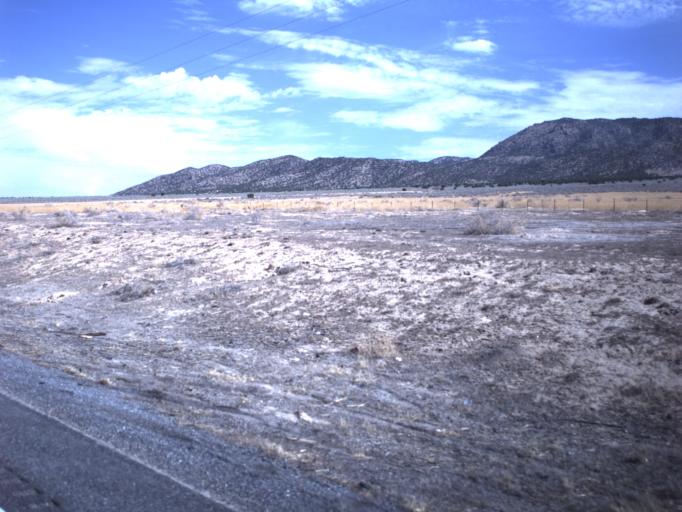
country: US
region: Utah
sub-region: Sanpete County
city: Gunnison
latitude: 39.2687
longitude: -111.8708
